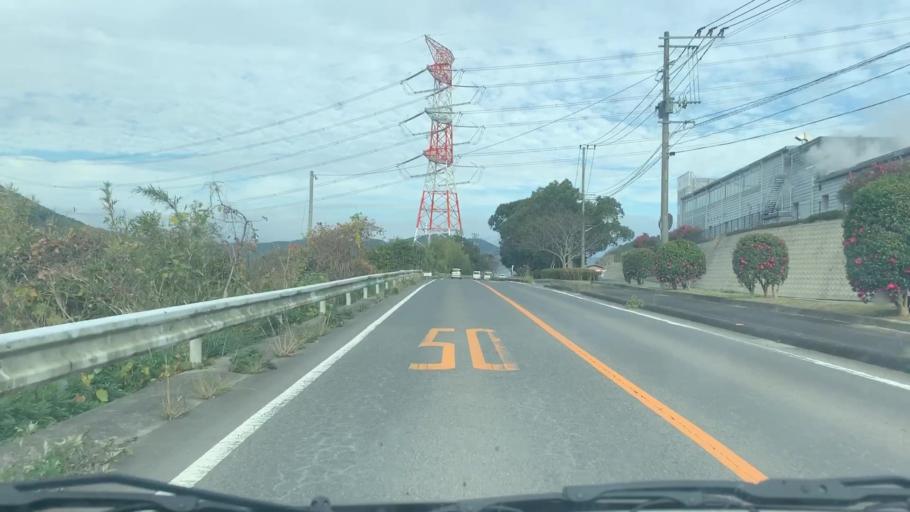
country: JP
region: Saga Prefecture
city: Karatsu
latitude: 33.3831
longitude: 129.9891
